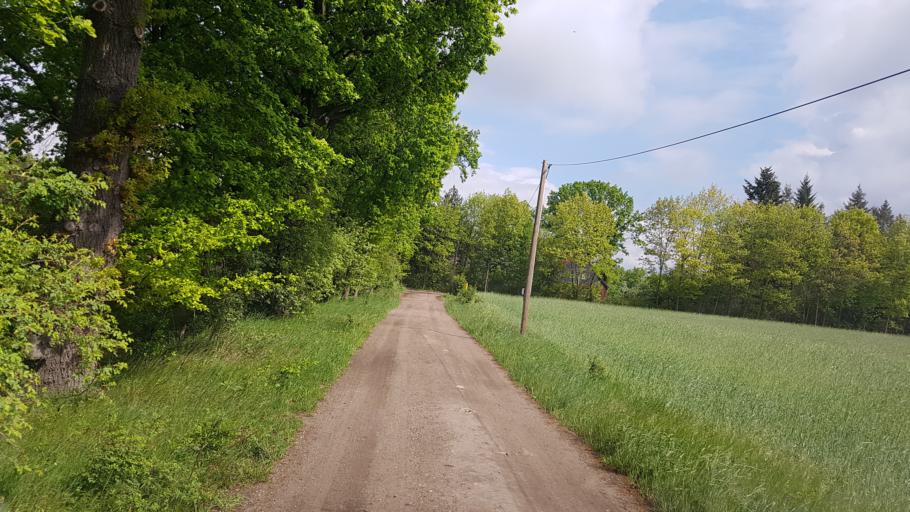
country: DE
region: Brandenburg
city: Elsterwerda
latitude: 51.4518
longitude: 13.5414
